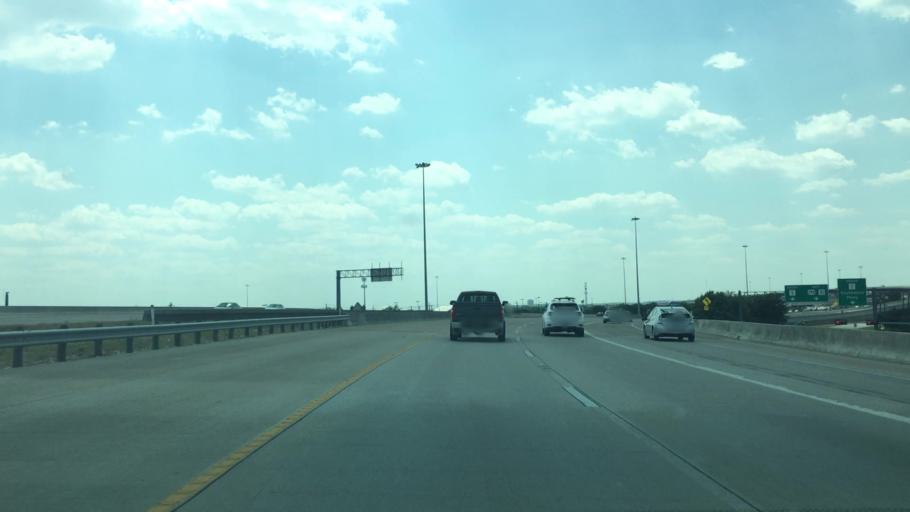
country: US
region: Texas
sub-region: Travis County
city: Rollingwood
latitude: 30.2337
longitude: -97.8174
